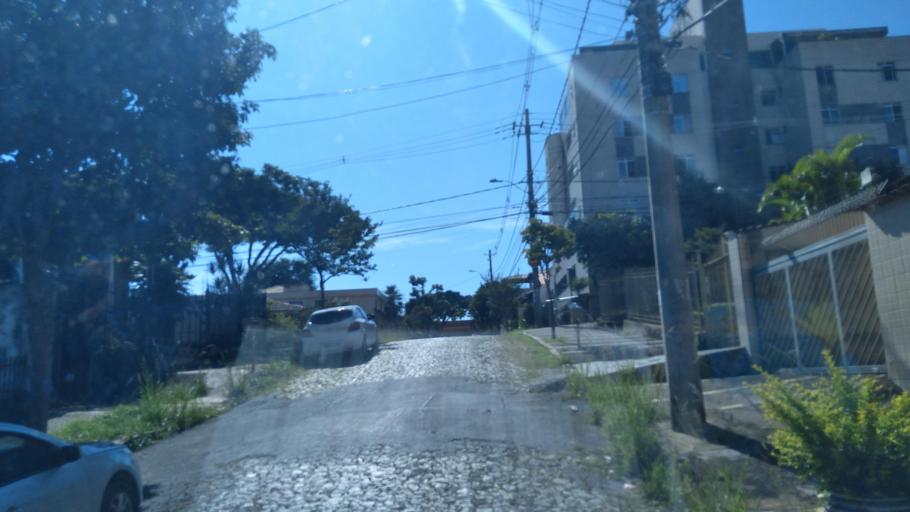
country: BR
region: Minas Gerais
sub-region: Belo Horizonte
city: Belo Horizonte
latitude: -19.8829
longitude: -43.9092
